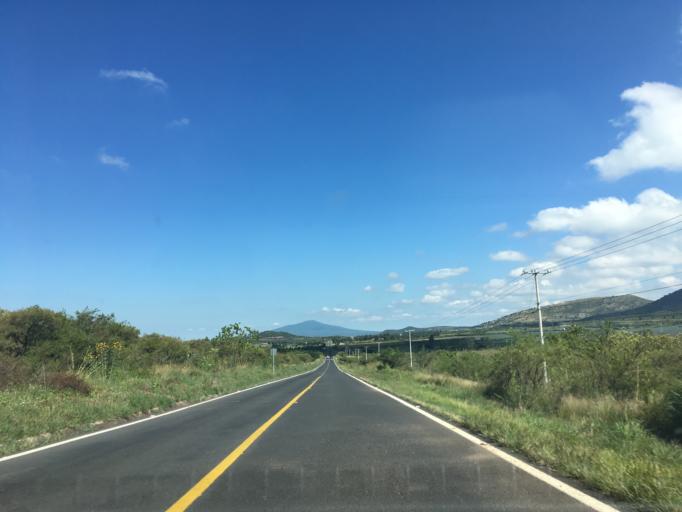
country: MX
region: Michoacan
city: Churintzio
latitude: 20.1065
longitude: -102.0637
